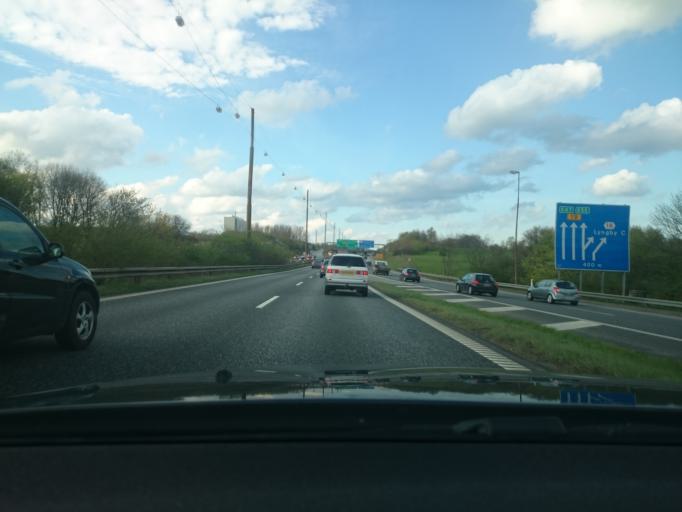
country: DK
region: Capital Region
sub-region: Lyngby-Tarbaek Kommune
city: Kongens Lyngby
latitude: 55.7696
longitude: 12.5237
